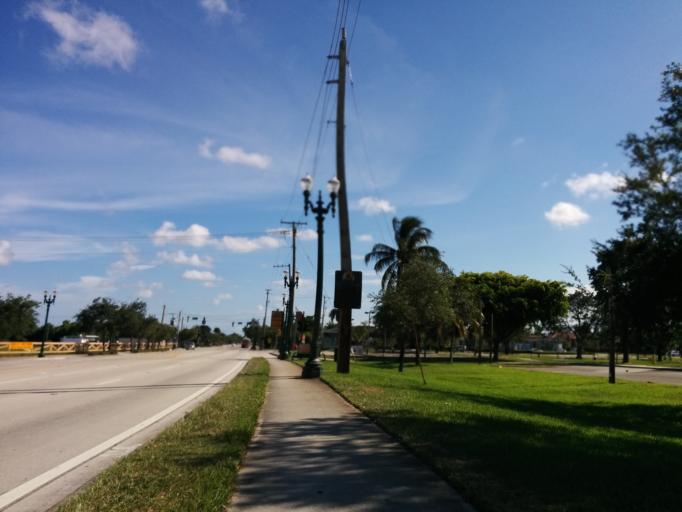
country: US
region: Florida
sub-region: Broward County
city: Davie
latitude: 26.0744
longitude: -80.2325
